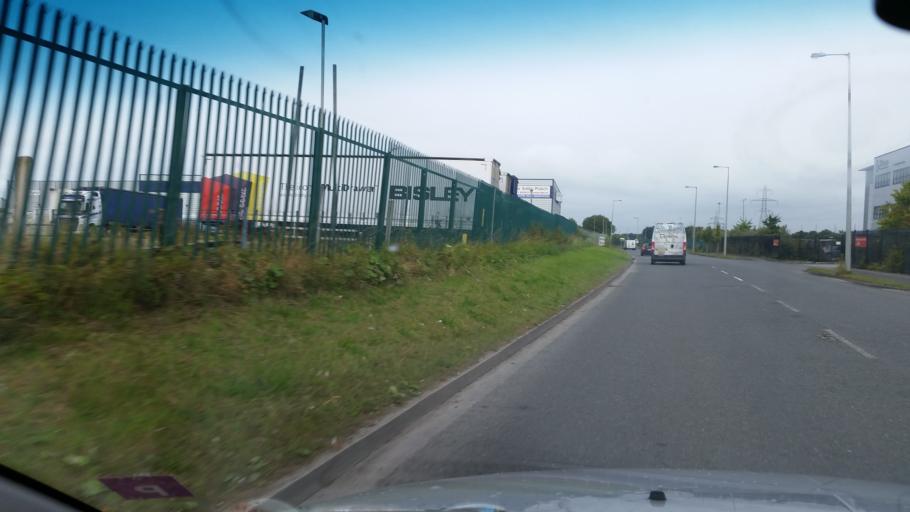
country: IE
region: Leinster
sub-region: Fingal County
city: Blanchardstown
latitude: 53.4139
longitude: -6.3526
